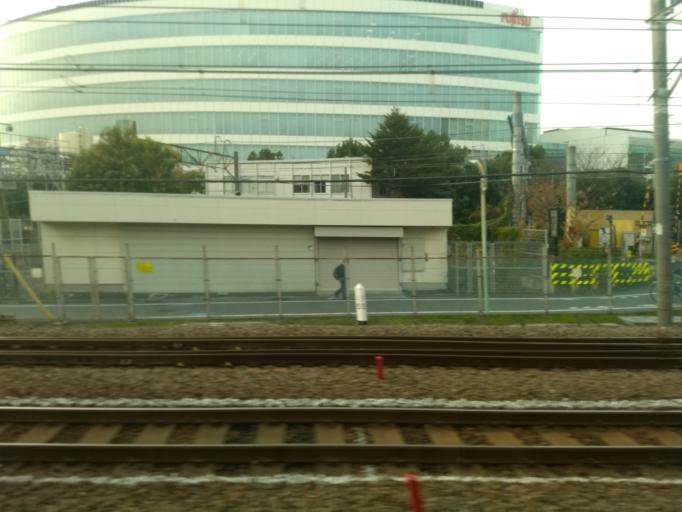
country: JP
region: Kanagawa
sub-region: Kawasaki-shi
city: Kawasaki
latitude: 35.5577
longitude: 139.7141
